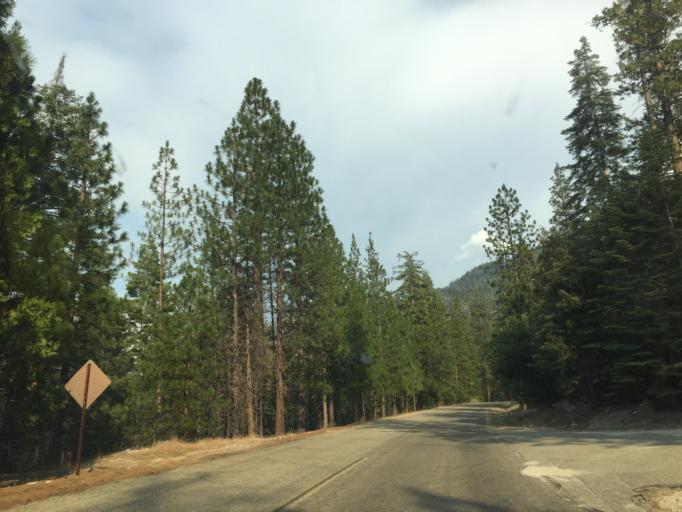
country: US
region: California
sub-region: Tulare County
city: Three Rivers
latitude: 36.7864
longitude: -118.6647
